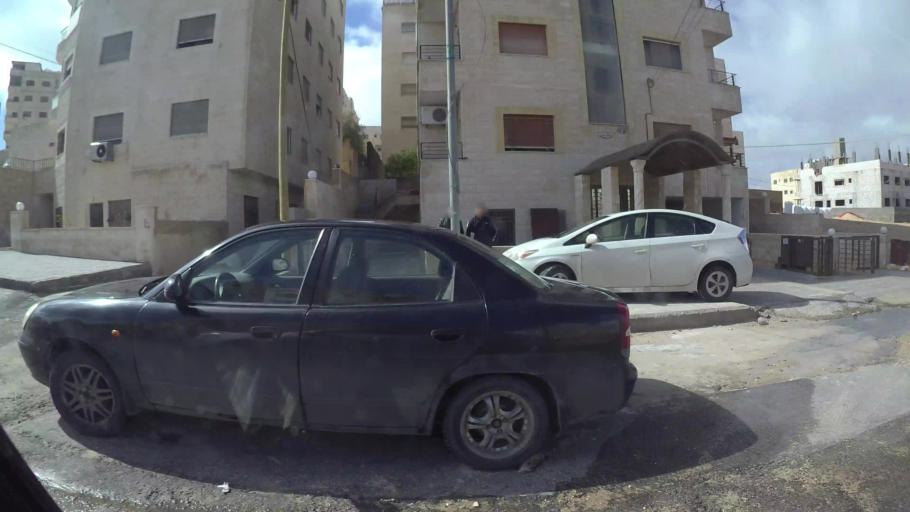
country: JO
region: Amman
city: Al Jubayhah
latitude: 32.0633
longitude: 35.8892
